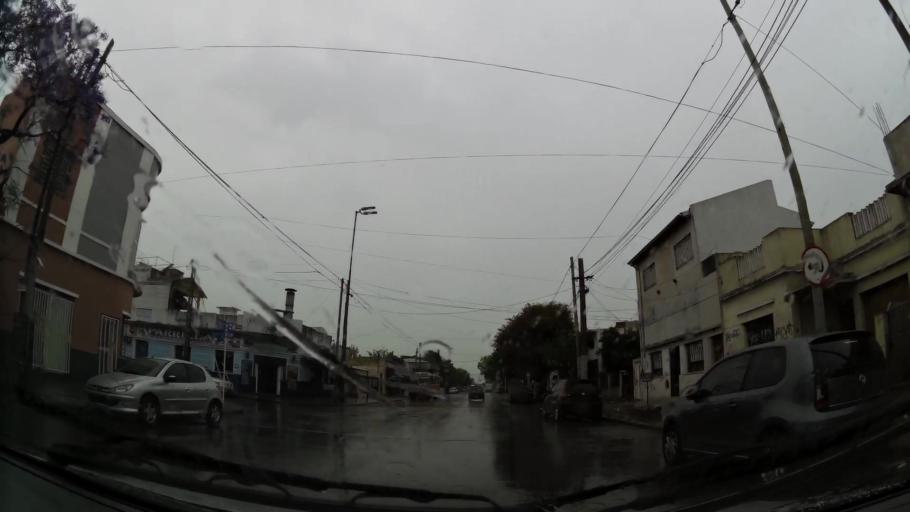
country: AR
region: Buenos Aires
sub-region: Partido de Lanus
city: Lanus
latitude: -34.7057
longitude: -58.4060
